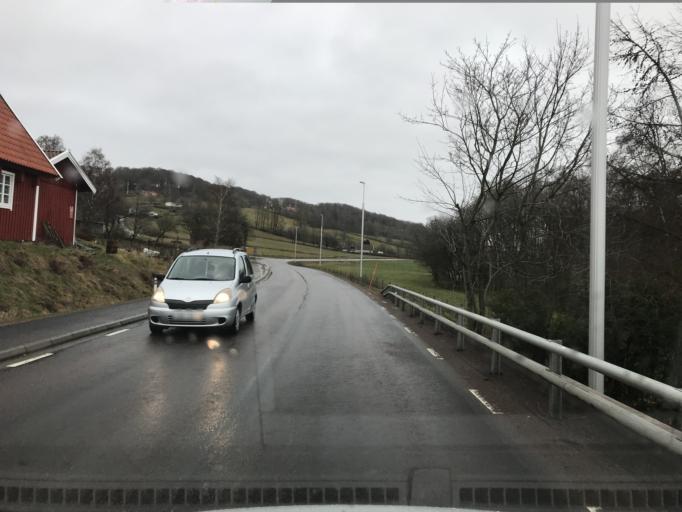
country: SE
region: Skane
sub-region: Bastads Kommun
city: Forslov
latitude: 56.3520
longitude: 12.8432
